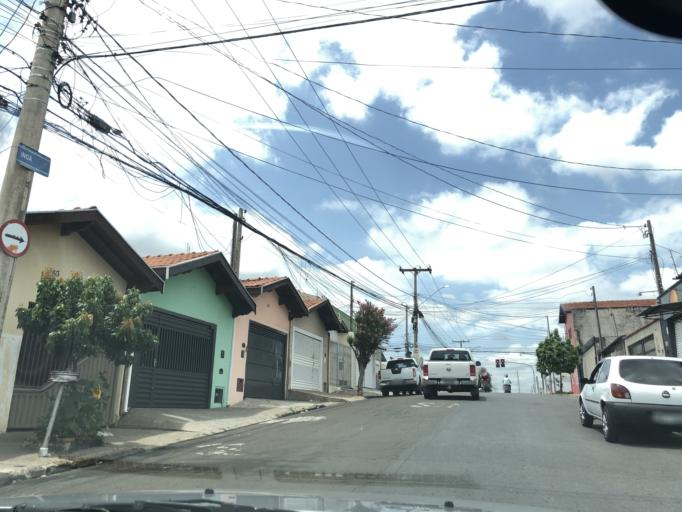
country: BR
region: Sao Paulo
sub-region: Piracicaba
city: Piracicaba
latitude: -22.7502
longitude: -47.6524
